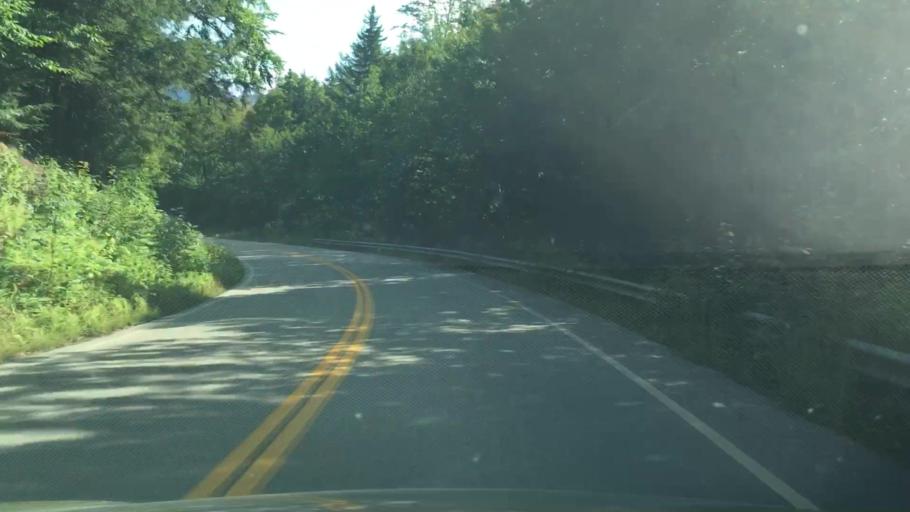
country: US
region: New Hampshire
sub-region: Carroll County
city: Tamworth
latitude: 44.0227
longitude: -71.3216
